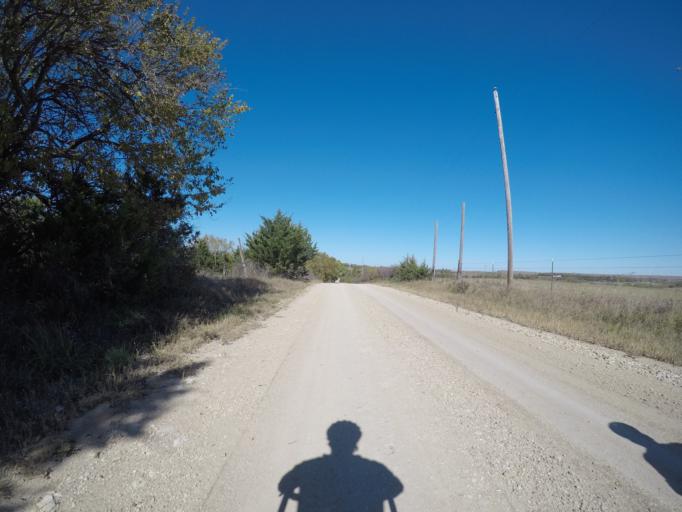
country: US
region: Kansas
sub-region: Wabaunsee County
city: Alma
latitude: 39.0487
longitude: -96.3582
